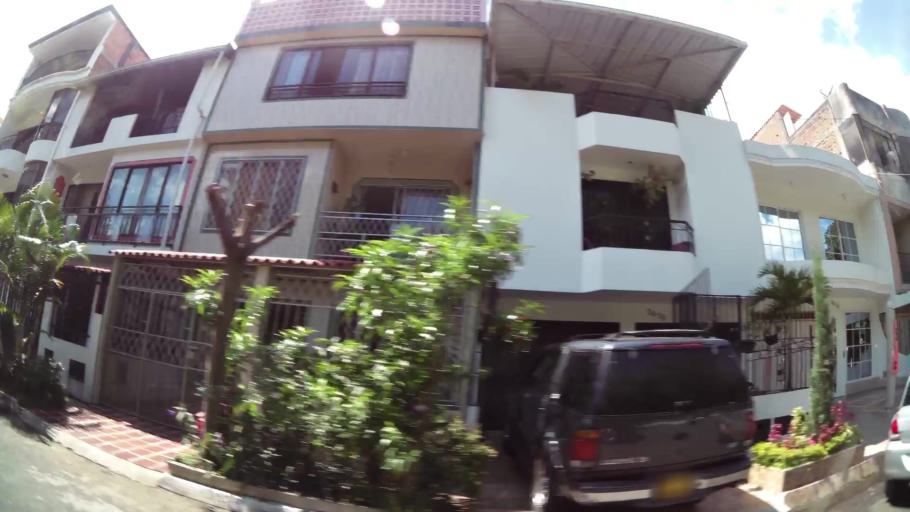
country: CO
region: Valle del Cauca
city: Cali
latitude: 3.3967
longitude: -76.5180
